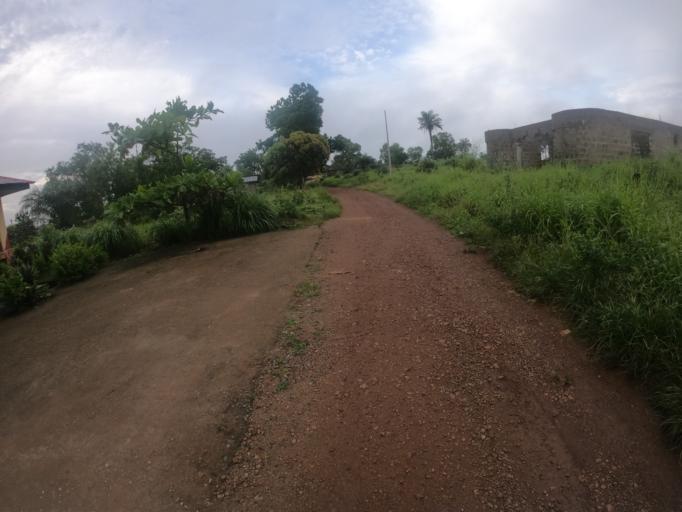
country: SL
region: Northern Province
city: Port Loko
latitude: 8.4966
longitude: -12.7510
